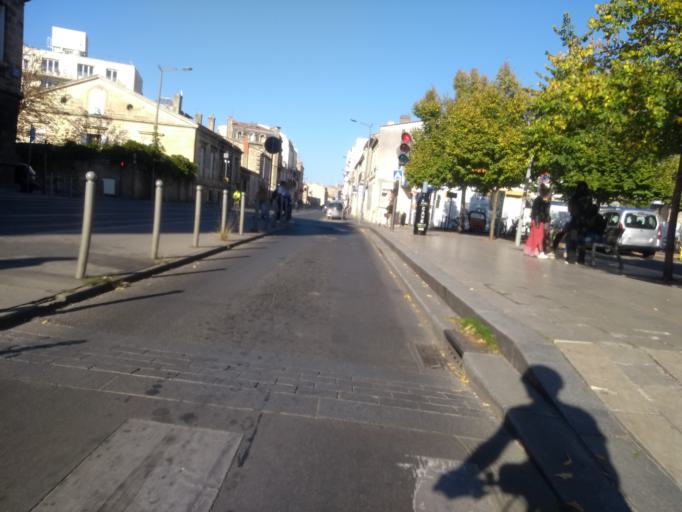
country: FR
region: Aquitaine
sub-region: Departement de la Gironde
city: Bordeaux
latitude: 44.8253
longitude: -0.5779
